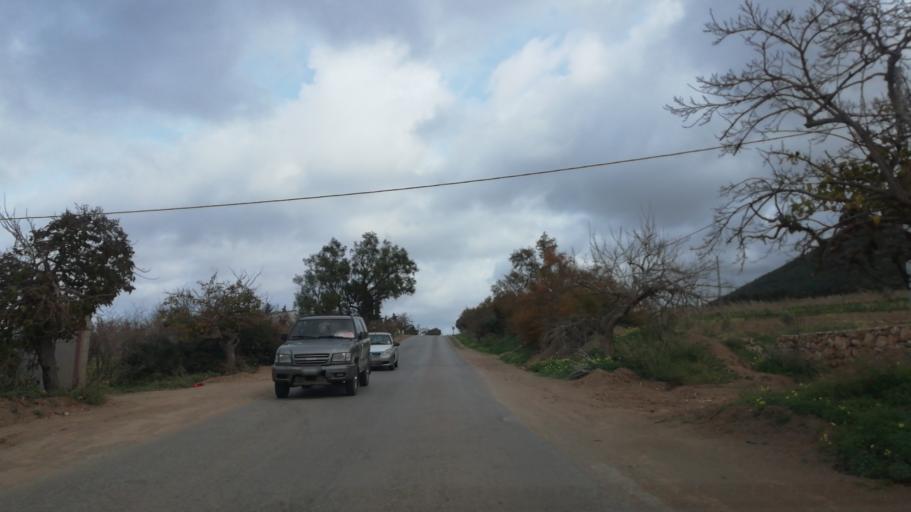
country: DZ
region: Oran
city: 'Ain el Turk
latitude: 35.7021
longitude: -0.8432
